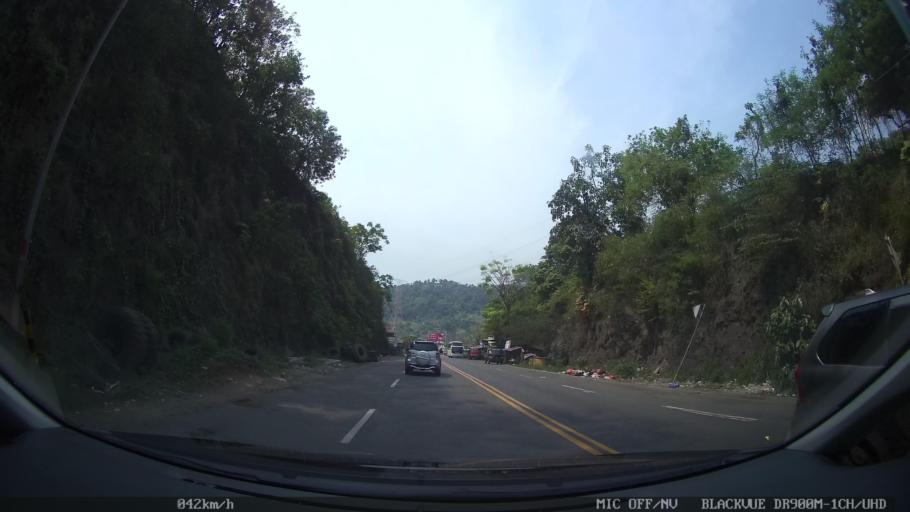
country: ID
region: Banten
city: Curug
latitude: -5.9459
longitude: 106.0040
